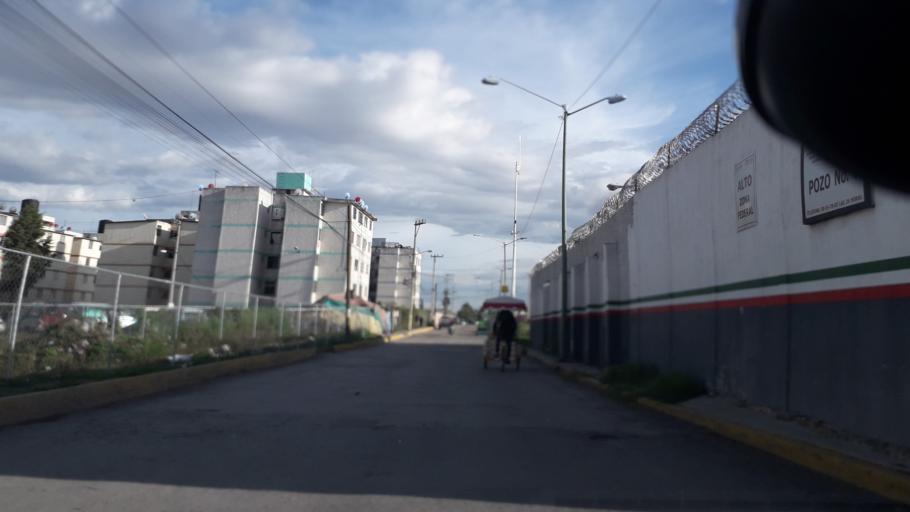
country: MX
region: Mexico
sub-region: Jaltenco
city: Alborada Jaltenco
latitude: 19.6638
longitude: -99.0726
